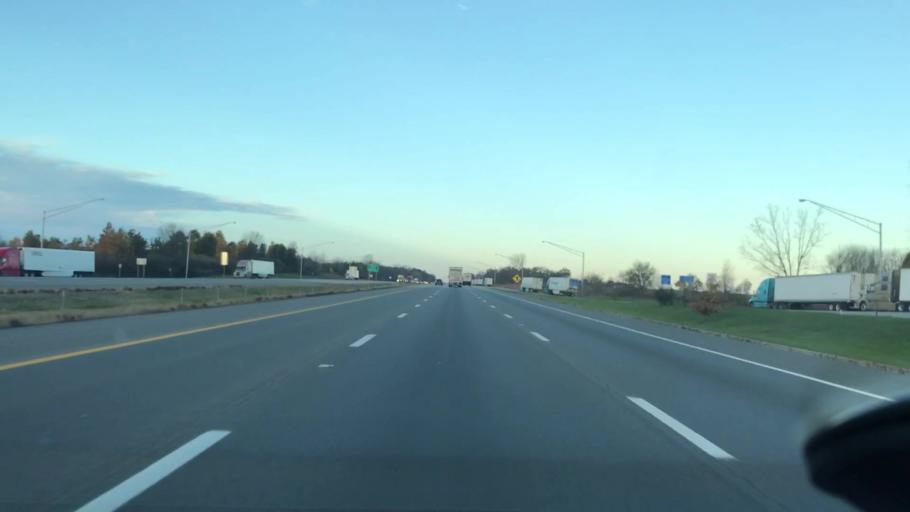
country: US
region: Ohio
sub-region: Madison County
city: Choctaw Lake
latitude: 39.9412
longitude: -83.5337
